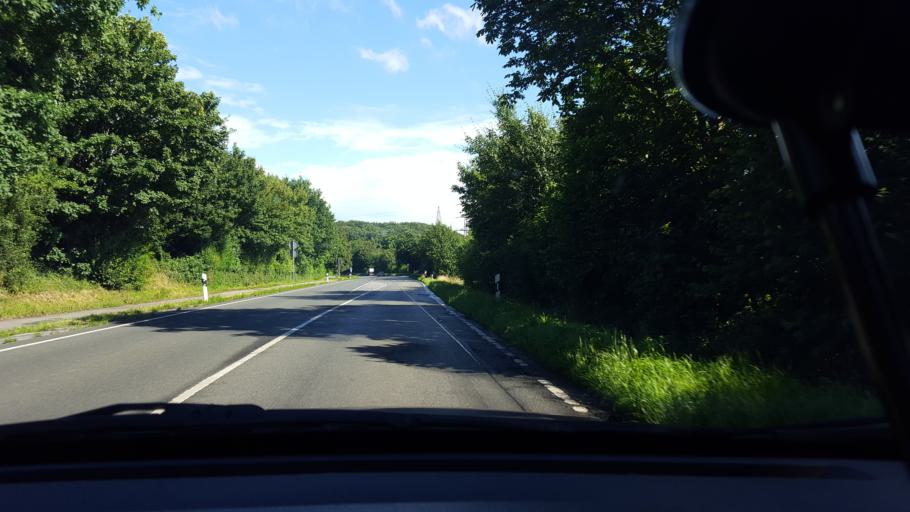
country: DE
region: North Rhine-Westphalia
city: Oer-Erkenschwick
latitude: 51.6561
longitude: 7.2199
